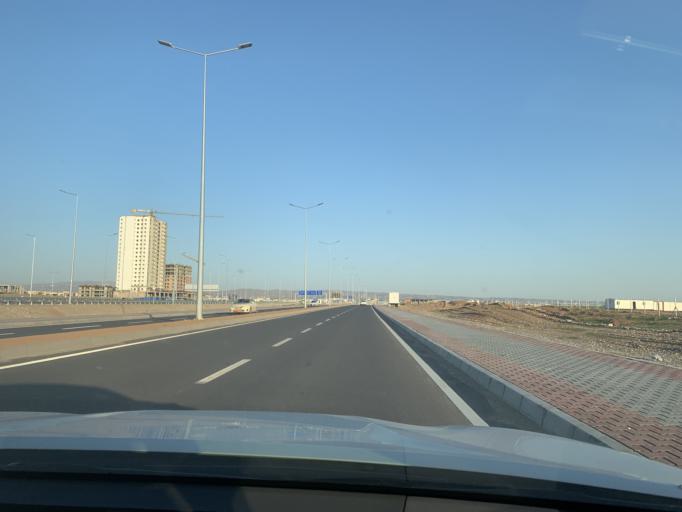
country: IQ
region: Arbil
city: Erbil
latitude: 36.2873
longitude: 44.0367
